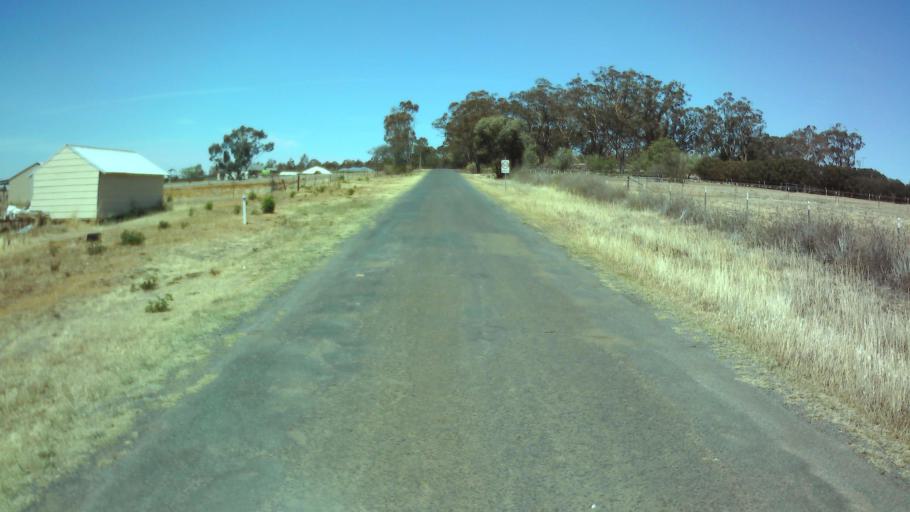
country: AU
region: New South Wales
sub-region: Weddin
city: Grenfell
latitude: -33.9007
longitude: 148.1730
